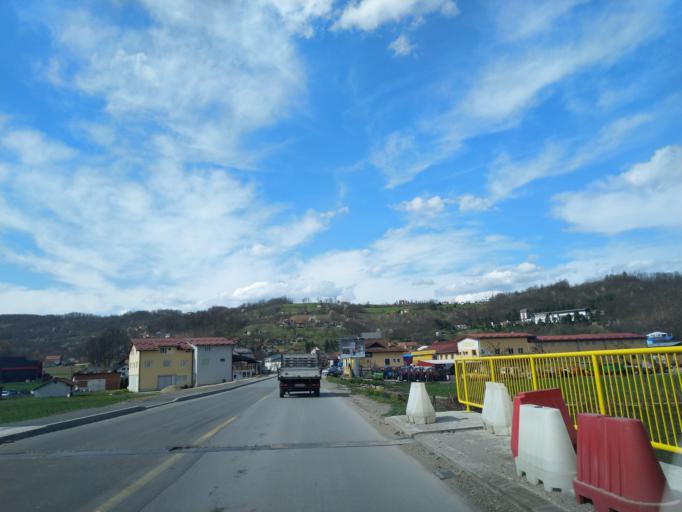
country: RS
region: Central Serbia
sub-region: Zlatiborski Okrug
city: Arilje
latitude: 43.7614
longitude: 20.0962
